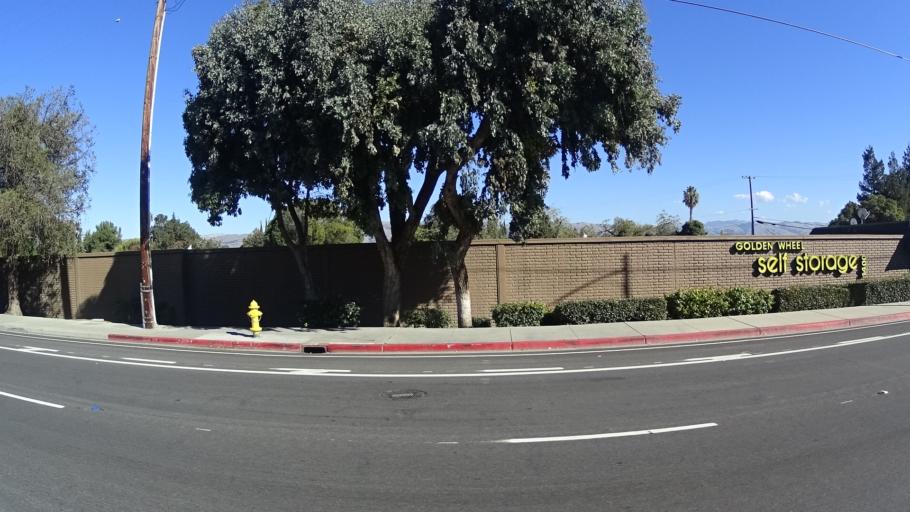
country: US
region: California
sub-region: Santa Clara County
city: San Jose
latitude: 37.3726
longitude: -121.8938
